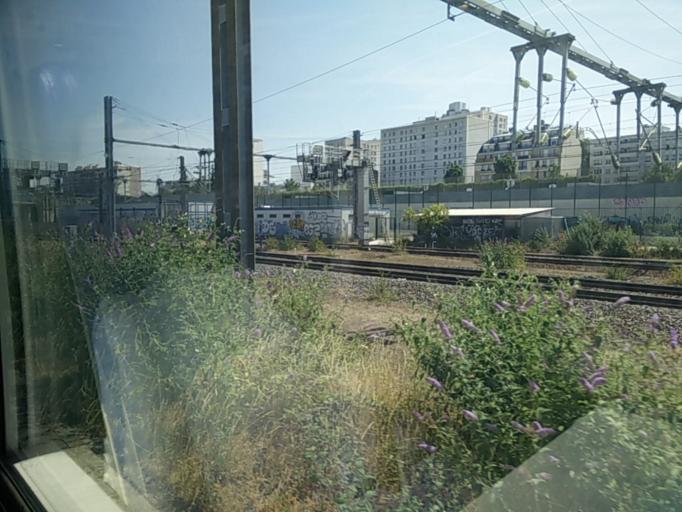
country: FR
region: Ile-de-France
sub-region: Departement de Seine-Saint-Denis
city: Aubervilliers
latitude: 48.8884
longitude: 2.3653
